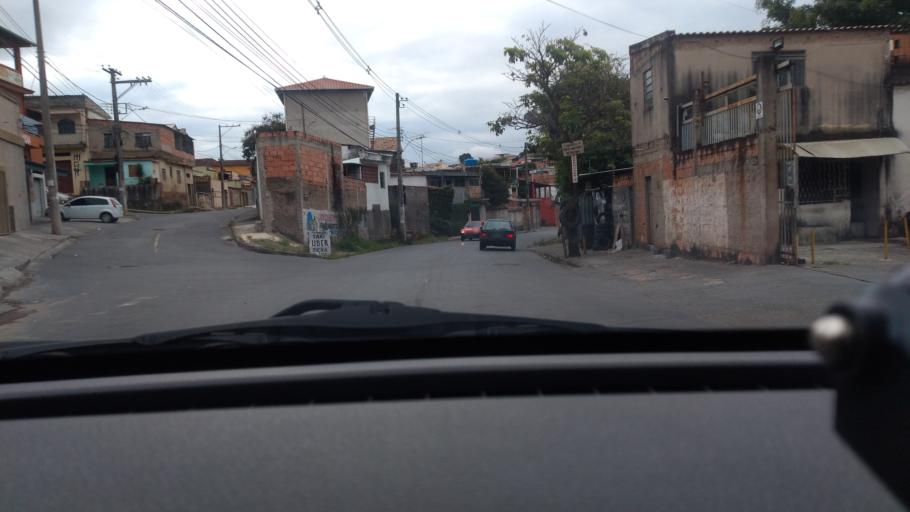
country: BR
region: Minas Gerais
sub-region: Belo Horizonte
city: Belo Horizonte
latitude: -19.8425
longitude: -43.9211
